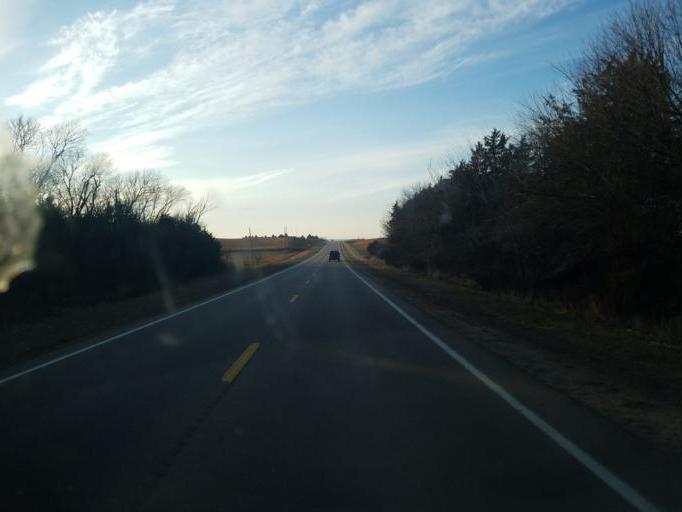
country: US
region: South Dakota
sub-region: Yankton County
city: Yankton
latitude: 42.7287
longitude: -97.4628
